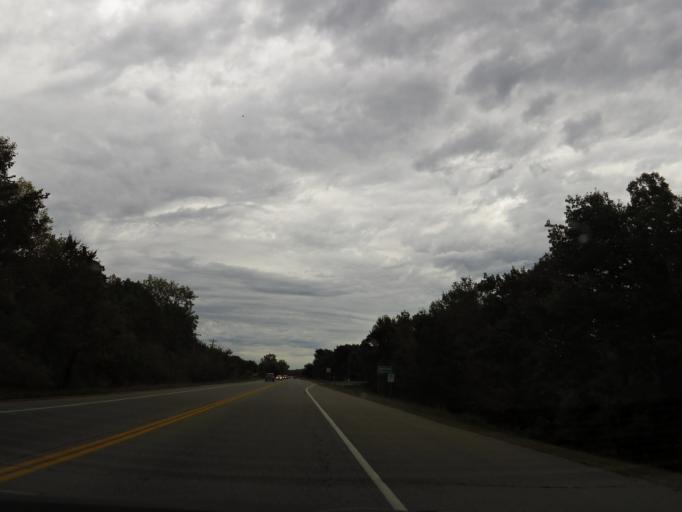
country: US
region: Minnesota
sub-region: Scott County
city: Prior Lake
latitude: 44.7272
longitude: -93.4001
